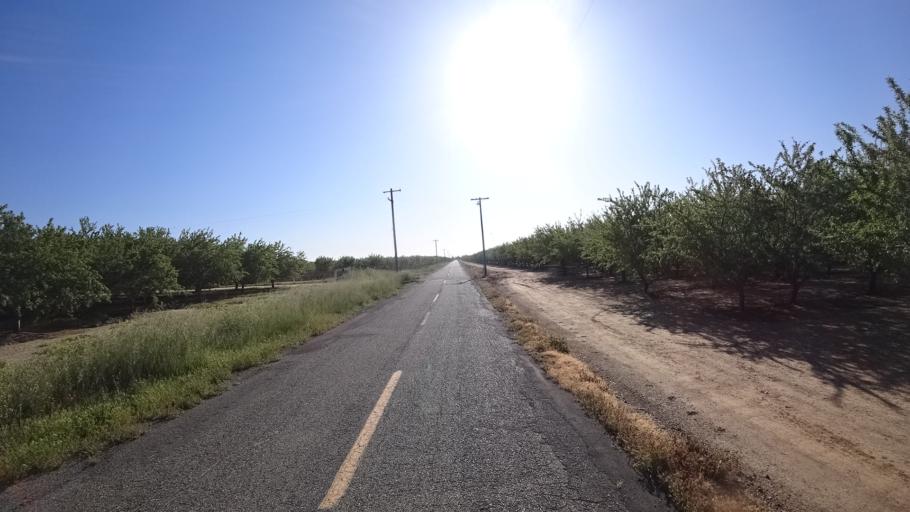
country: US
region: California
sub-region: Glenn County
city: Orland
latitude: 39.6960
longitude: -122.1132
